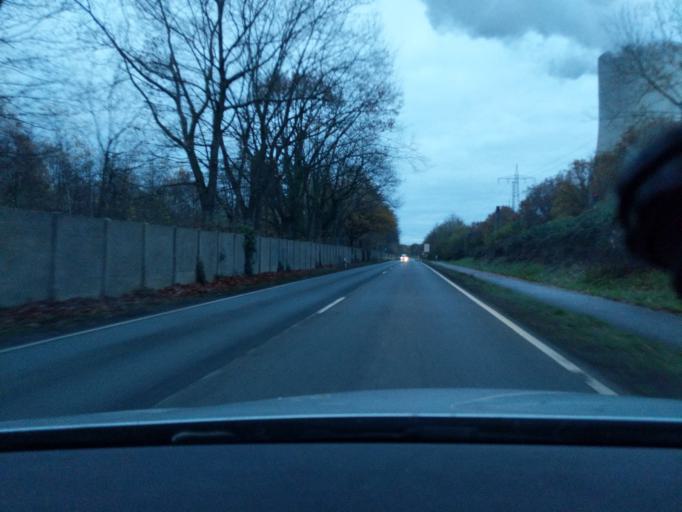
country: DE
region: North Rhine-Westphalia
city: Waltrop
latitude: 51.6179
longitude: 7.4589
